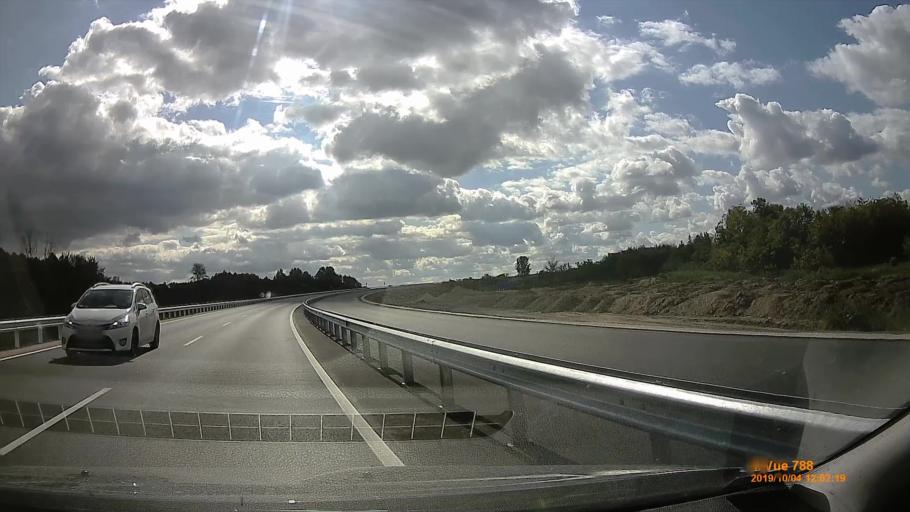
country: HU
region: Somogy
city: Karad
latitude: 46.6023
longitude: 17.8020
